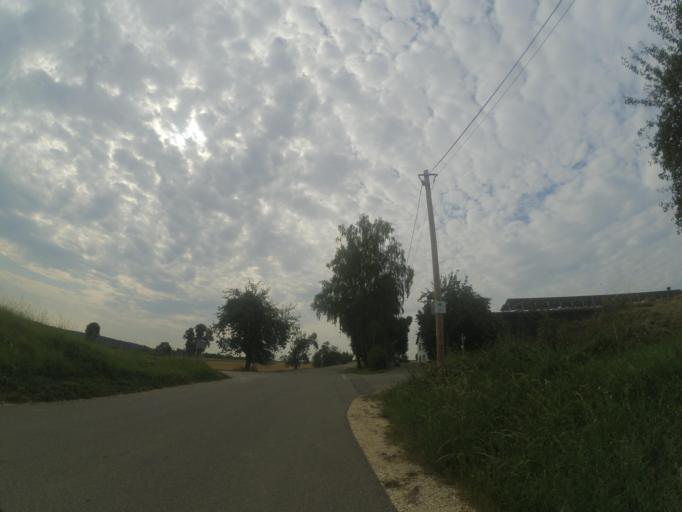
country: DE
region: Baden-Wuerttemberg
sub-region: Tuebingen Region
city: Westerstetten
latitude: 48.5188
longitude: 9.9459
